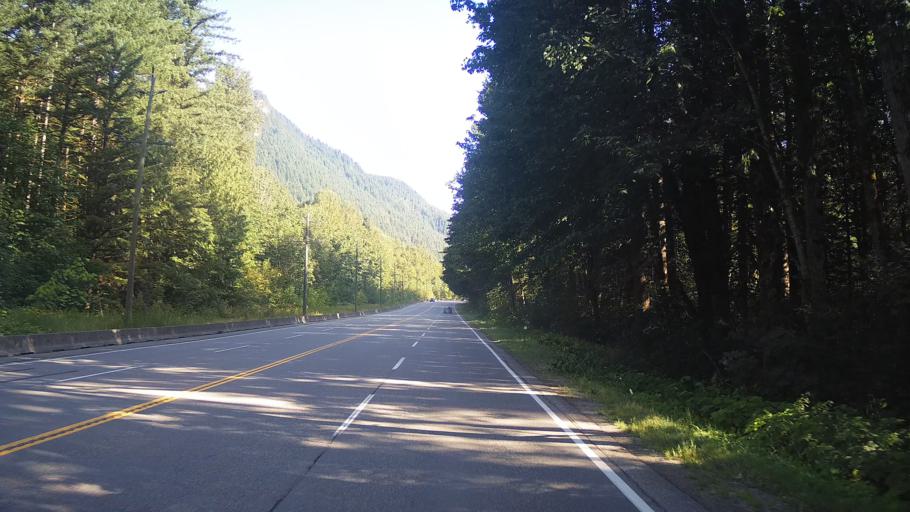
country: CA
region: British Columbia
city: Hope
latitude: 49.4445
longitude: -121.4368
